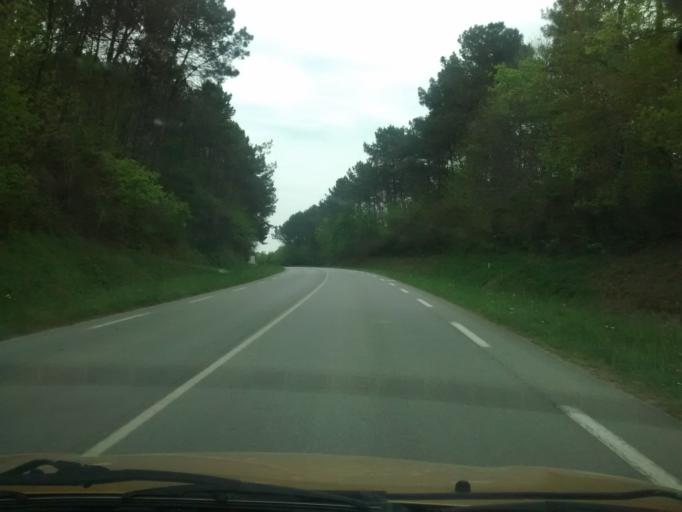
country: FR
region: Brittany
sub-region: Departement du Morbihan
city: Berric
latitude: 47.6085
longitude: -2.5410
